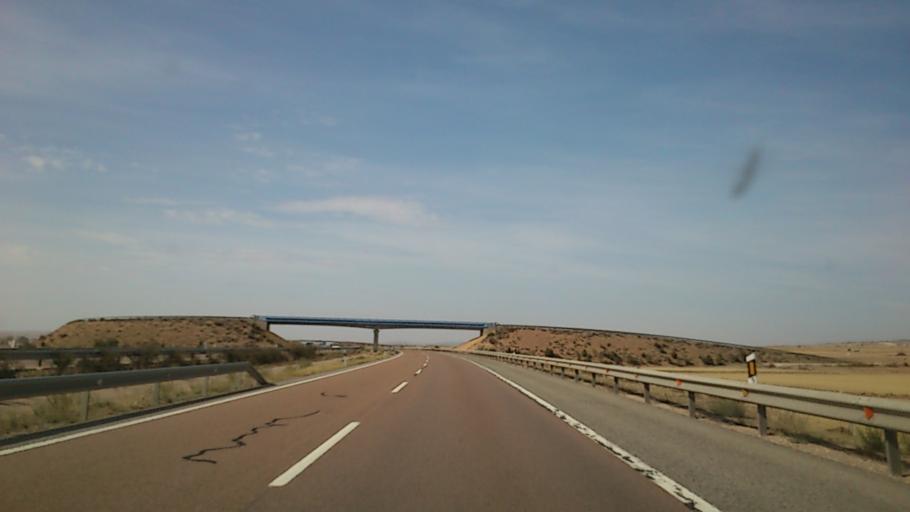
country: ES
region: Aragon
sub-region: Provincia de Teruel
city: Singra
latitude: 40.6772
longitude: -1.3141
